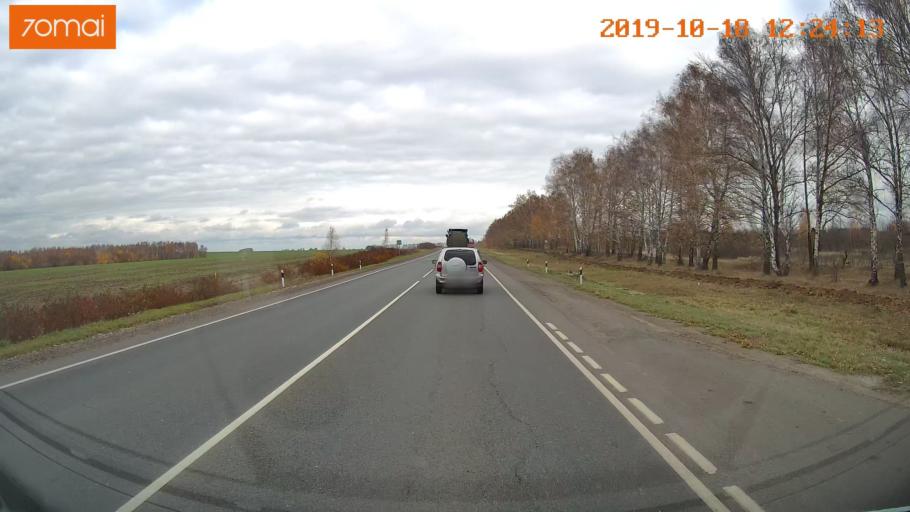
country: RU
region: Rjazan
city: Rybnoye
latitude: 54.5372
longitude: 39.5124
